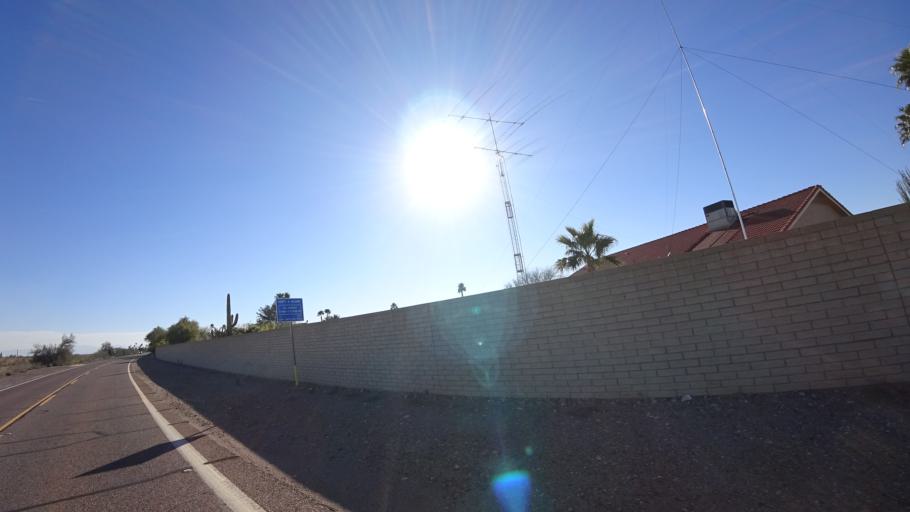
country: US
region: Arizona
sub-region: Maricopa County
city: Sun City West
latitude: 33.6807
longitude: -112.3255
